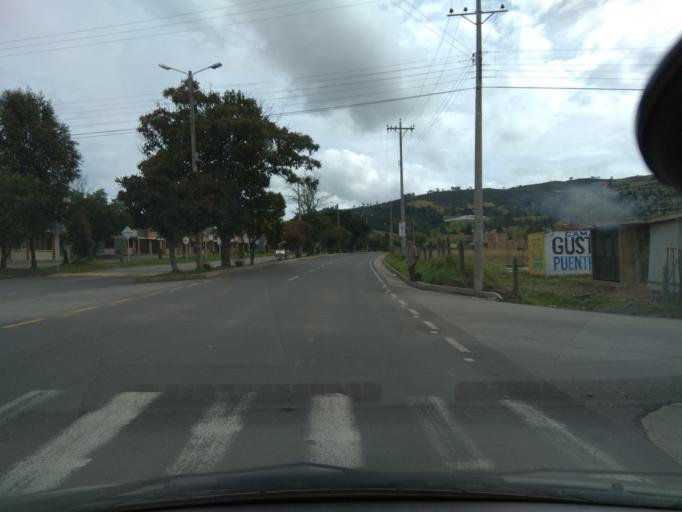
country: CO
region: Boyaca
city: Santa Rosa de Viterbo
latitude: 5.8806
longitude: -72.9832
